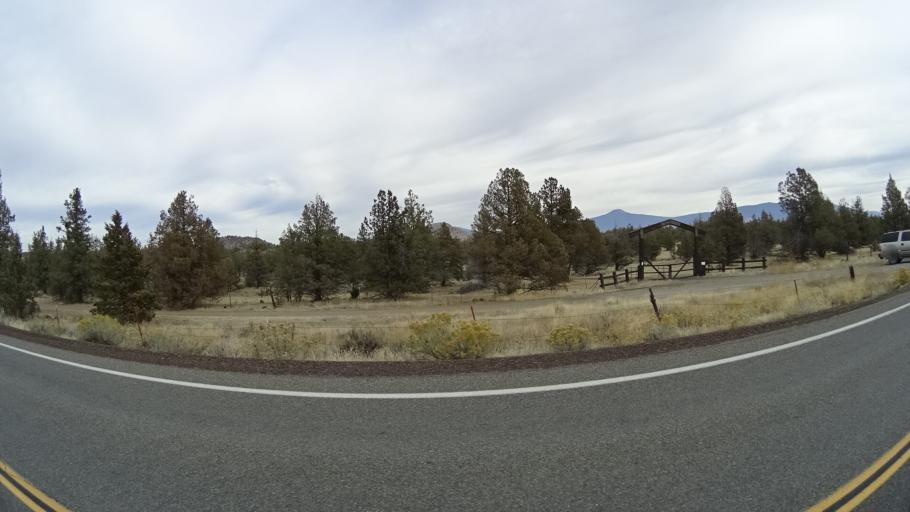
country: US
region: California
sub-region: Siskiyou County
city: Montague
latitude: 41.6376
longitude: -122.4567
